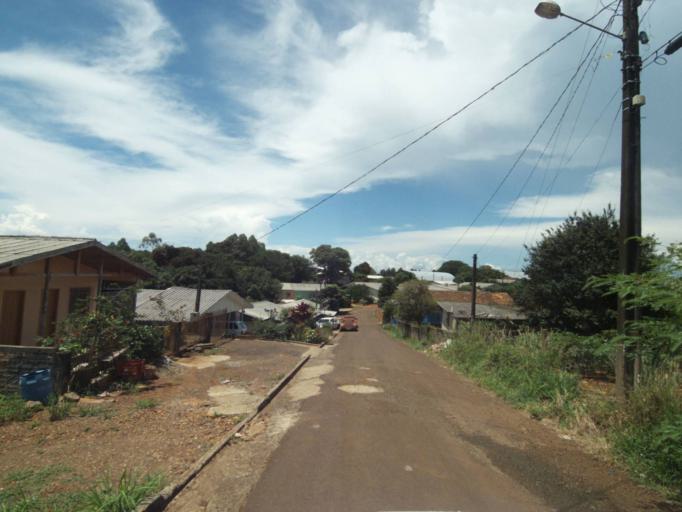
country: BR
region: Parana
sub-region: Guaraniacu
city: Guaraniacu
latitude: -25.0938
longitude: -52.8754
